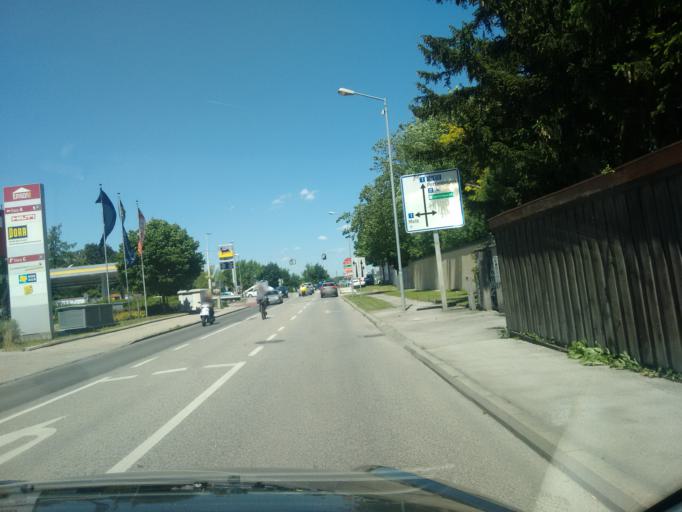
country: AT
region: Lower Austria
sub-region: Sankt Polten Stadt
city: Sankt Poelten
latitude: 48.2026
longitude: 15.6384
